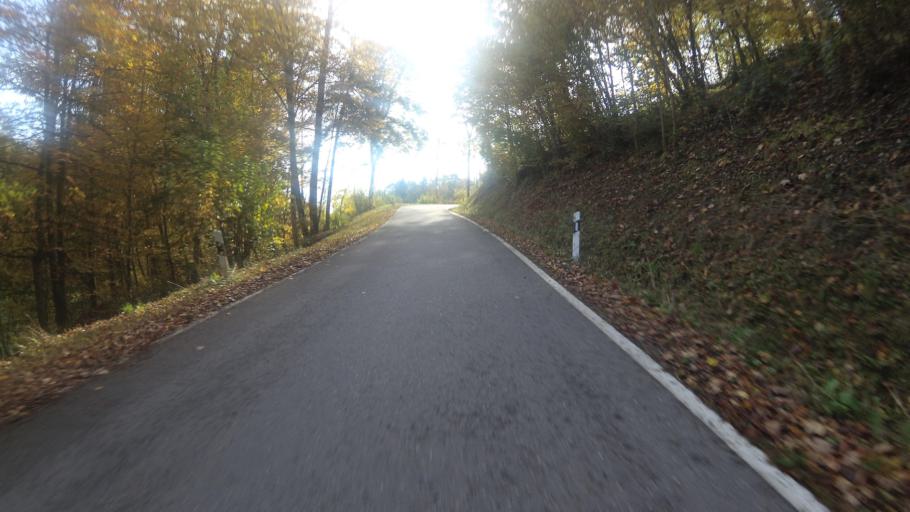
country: DE
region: Baden-Wuerttemberg
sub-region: Regierungsbezirk Stuttgart
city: Neudenau
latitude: 49.3167
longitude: 9.2977
